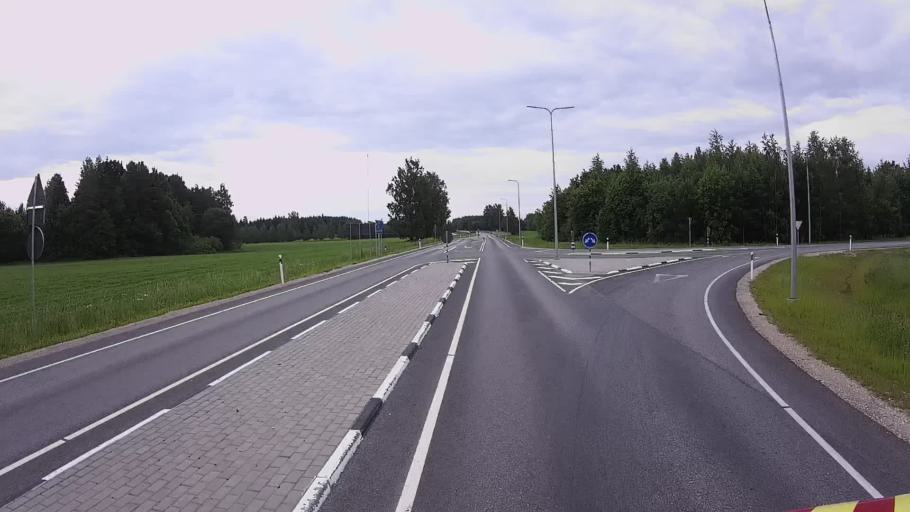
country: EE
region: Viljandimaa
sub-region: Viljandi linn
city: Viljandi
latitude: 58.2416
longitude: 25.5946
